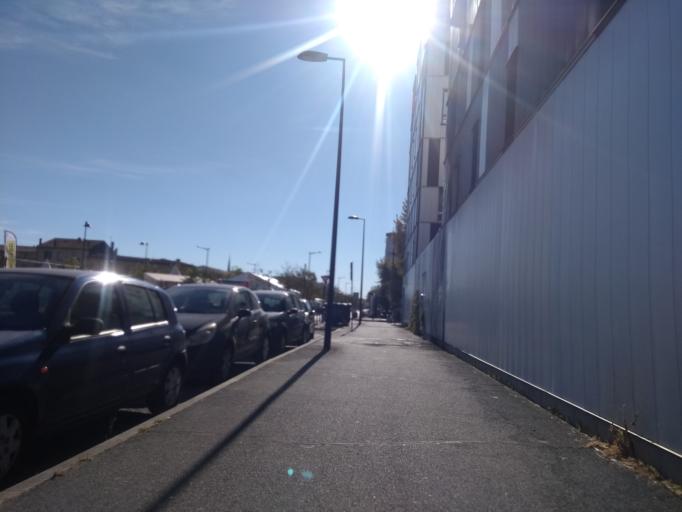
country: FR
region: Aquitaine
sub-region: Departement de la Gironde
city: Bordeaux
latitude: 44.8445
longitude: -0.5570
